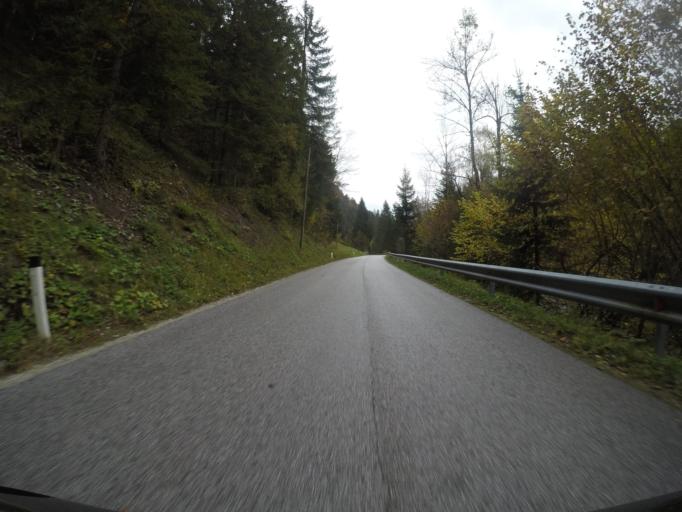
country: SI
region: Gorje
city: Zgornje Gorje
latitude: 46.3818
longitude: 14.0478
